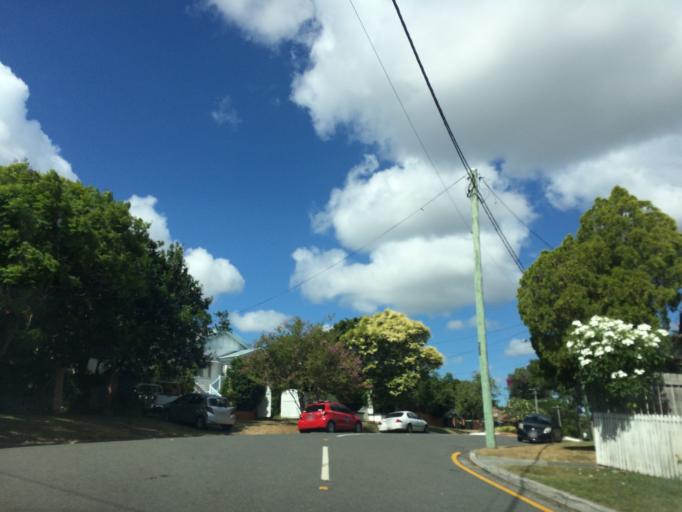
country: AU
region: Queensland
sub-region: Brisbane
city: Woolloongabba
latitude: -27.4900
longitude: 153.0476
